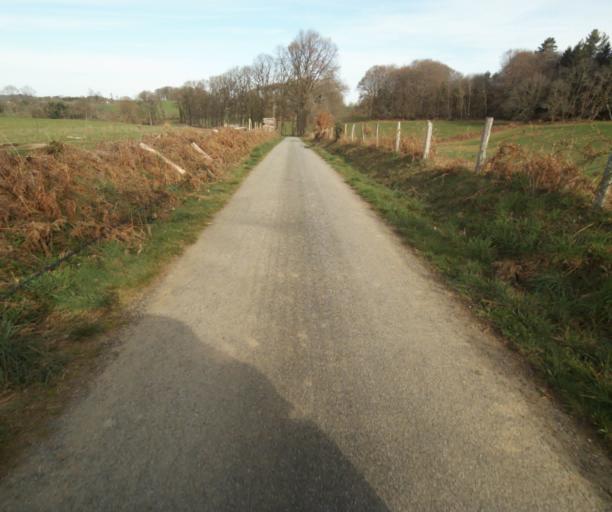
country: FR
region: Limousin
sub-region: Departement de la Correze
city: Chamboulive
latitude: 45.4267
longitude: 1.7519
